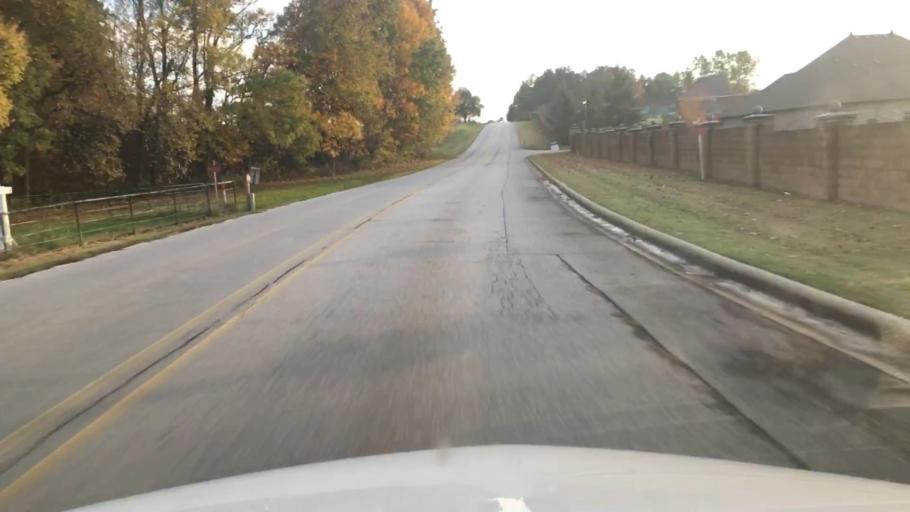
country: US
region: Arkansas
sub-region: Washington County
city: Tontitown
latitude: 36.1875
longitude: -94.2318
